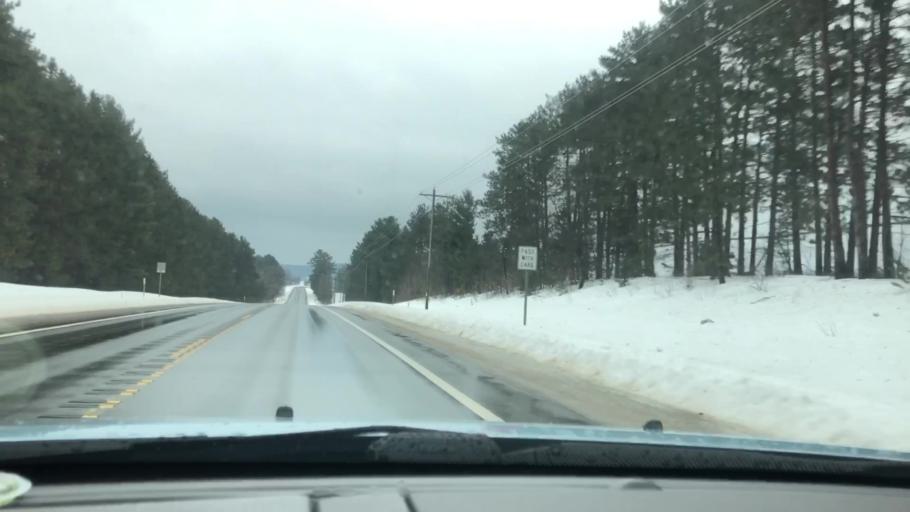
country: US
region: Michigan
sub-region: Charlevoix County
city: Boyne City
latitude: 45.0945
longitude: -84.9669
